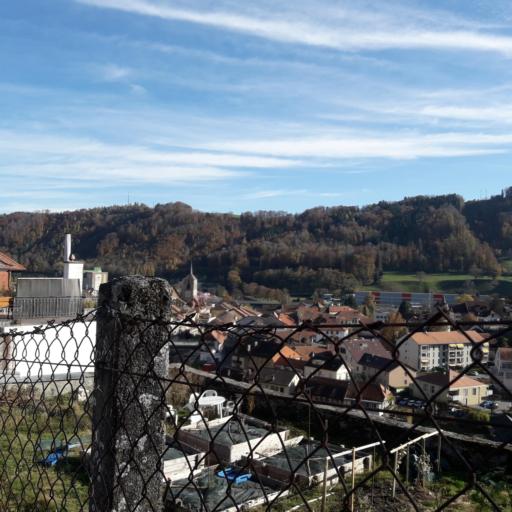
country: CH
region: Vaud
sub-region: Broye-Vully District
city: Moudon
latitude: 46.6692
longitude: 6.7936
